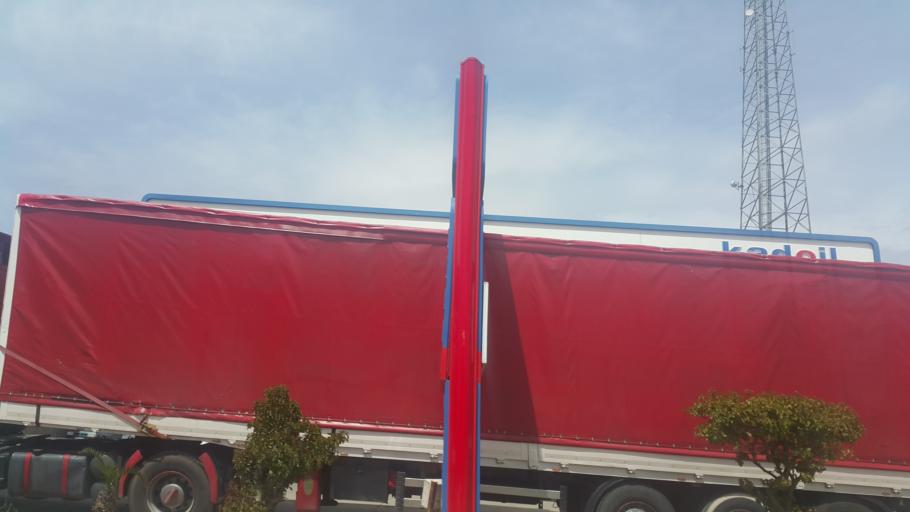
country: TR
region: Adana
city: Yakapinar
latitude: 36.9657
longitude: 35.6096
